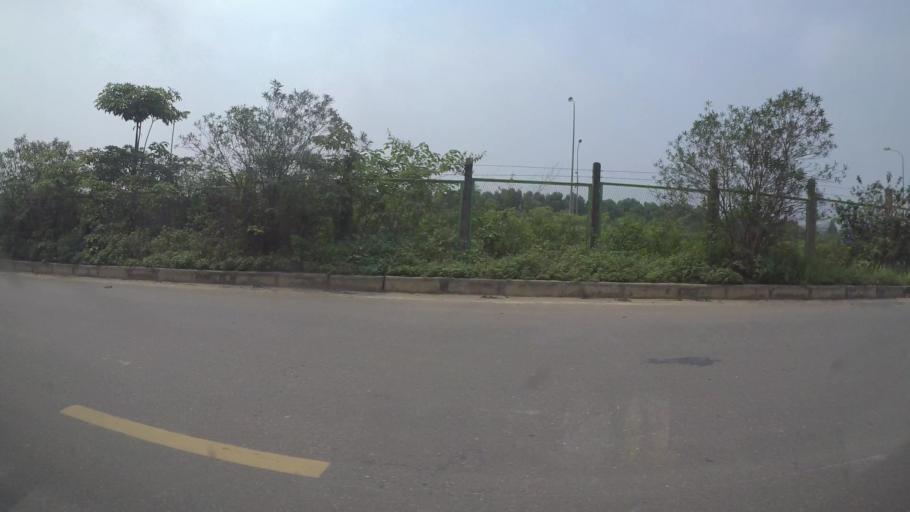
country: VN
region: Ha Noi
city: Lien Quan
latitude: 20.9907
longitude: 105.5535
